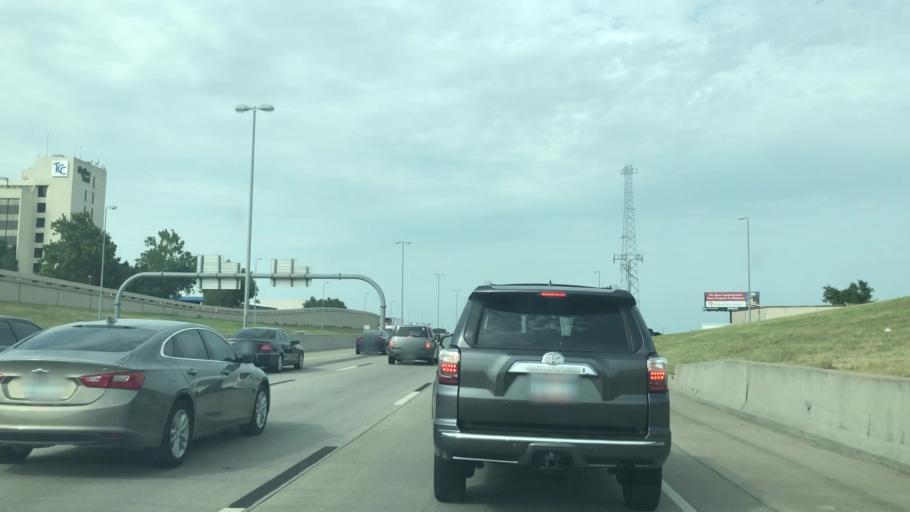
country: US
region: Oklahoma
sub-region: Tulsa County
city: Tulsa
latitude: 36.1047
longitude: -95.9088
